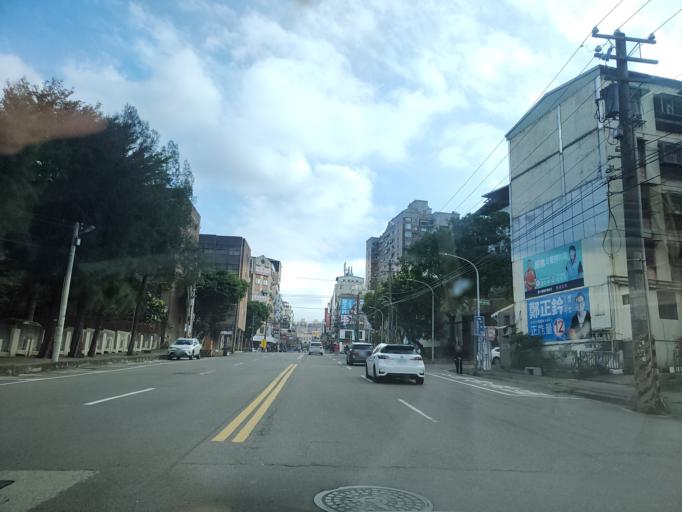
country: TW
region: Taiwan
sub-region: Hsinchu
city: Hsinchu
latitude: 24.7997
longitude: 120.9974
